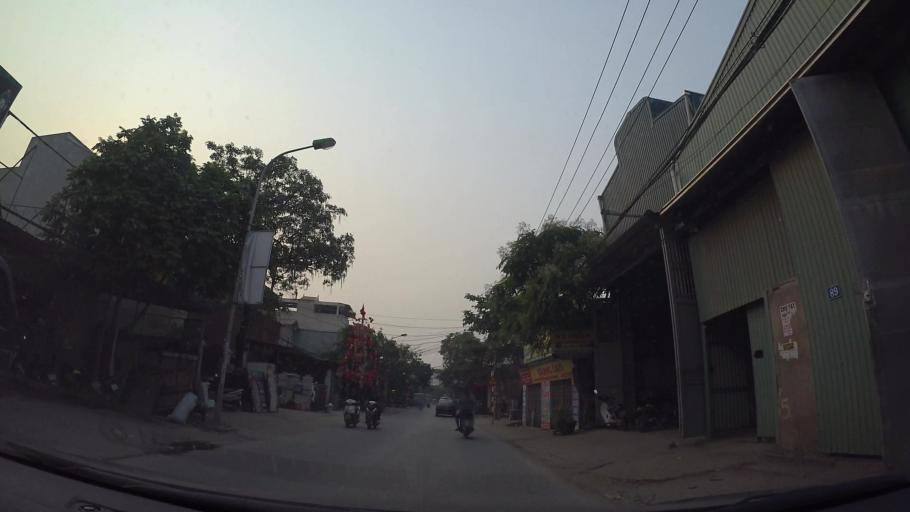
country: VN
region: Ha Noi
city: Kim Bai
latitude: 20.8698
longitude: 105.8064
